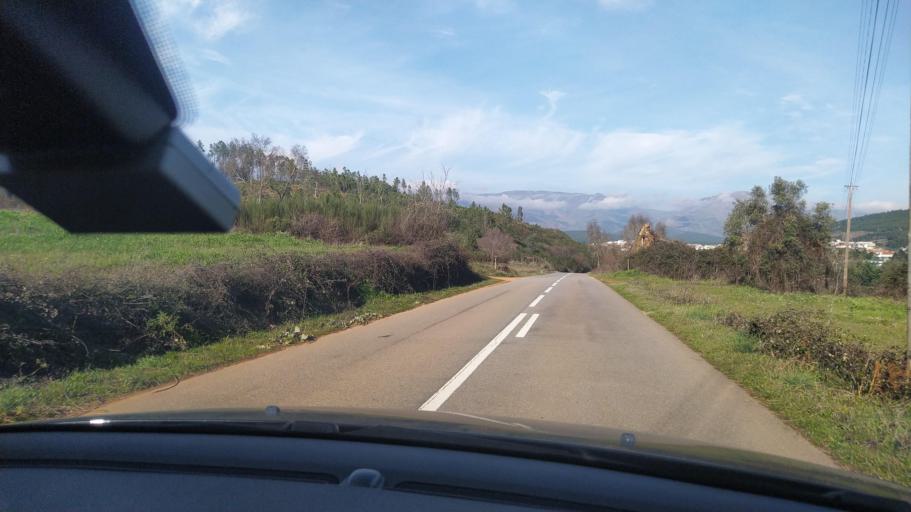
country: PT
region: Castelo Branco
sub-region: Concelho do Fundao
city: Aldeia de Joanes
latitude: 40.1853
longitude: -7.6440
